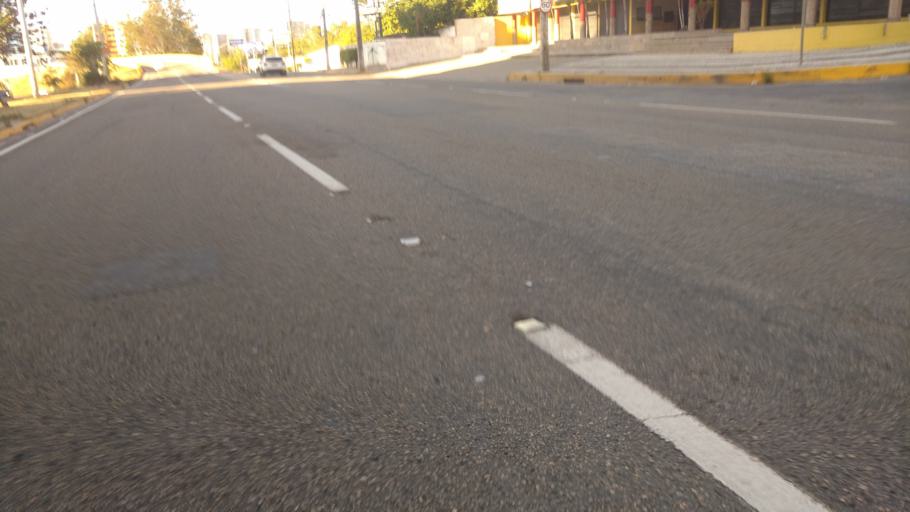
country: BR
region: Ceara
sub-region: Fortaleza
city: Fortaleza
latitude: -3.7610
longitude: -38.4829
